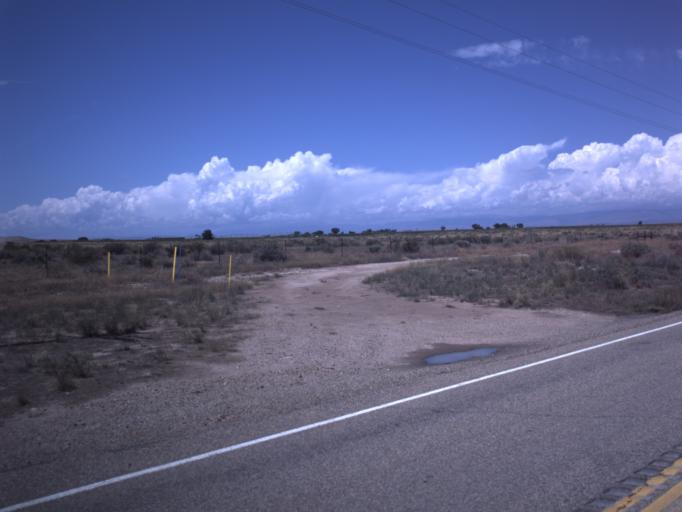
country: US
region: Utah
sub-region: Uintah County
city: Naples
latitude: 40.1326
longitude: -109.6638
